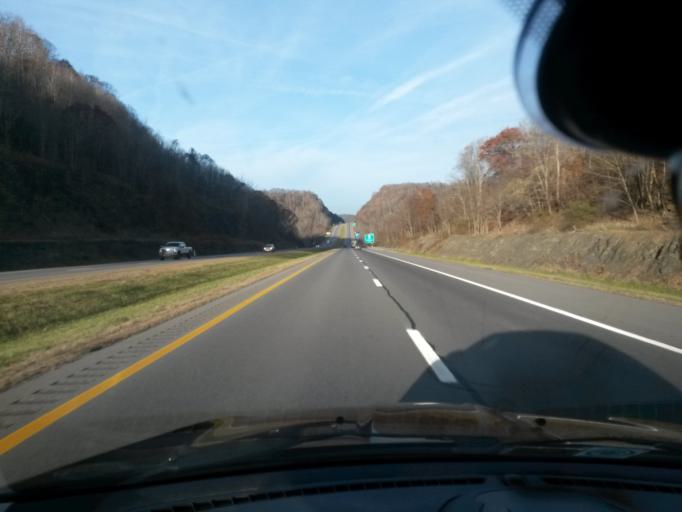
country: US
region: West Virginia
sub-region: Greenbrier County
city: Lewisburg
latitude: 37.8611
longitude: -80.5302
